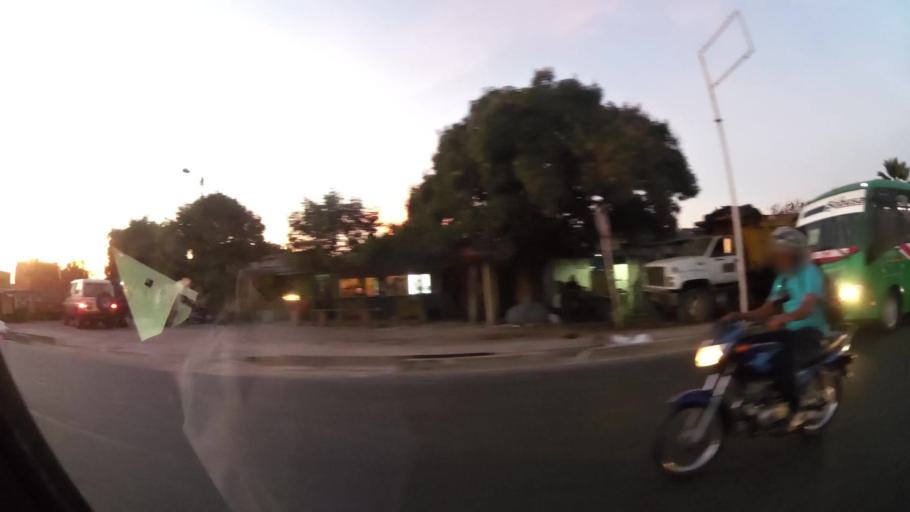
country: CO
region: Atlantico
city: Soledad
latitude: 10.9324
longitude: -74.7822
